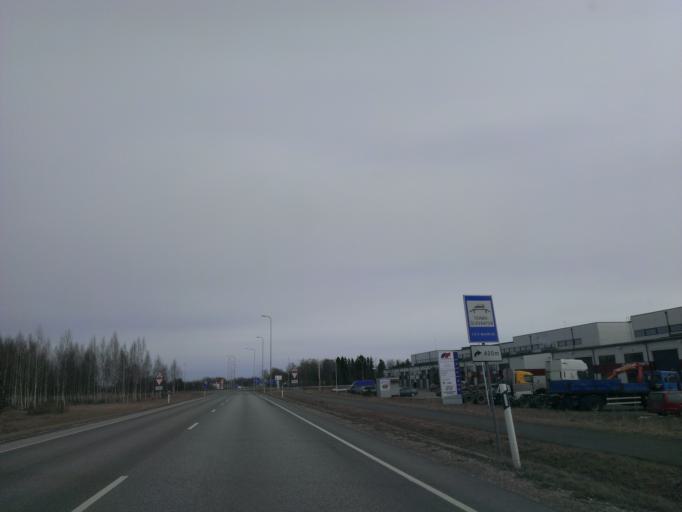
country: EE
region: Paernumaa
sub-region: Paernu linn
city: Parnu
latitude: 58.3978
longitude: 24.4440
